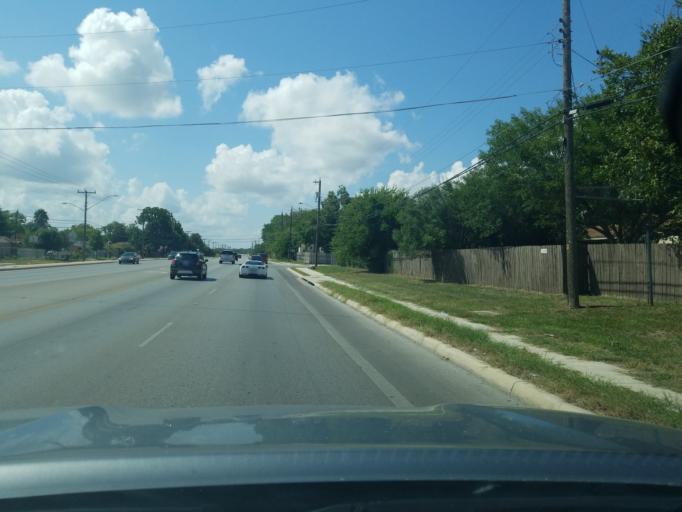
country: US
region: Texas
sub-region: Bexar County
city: San Antonio
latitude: 29.3449
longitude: -98.5342
